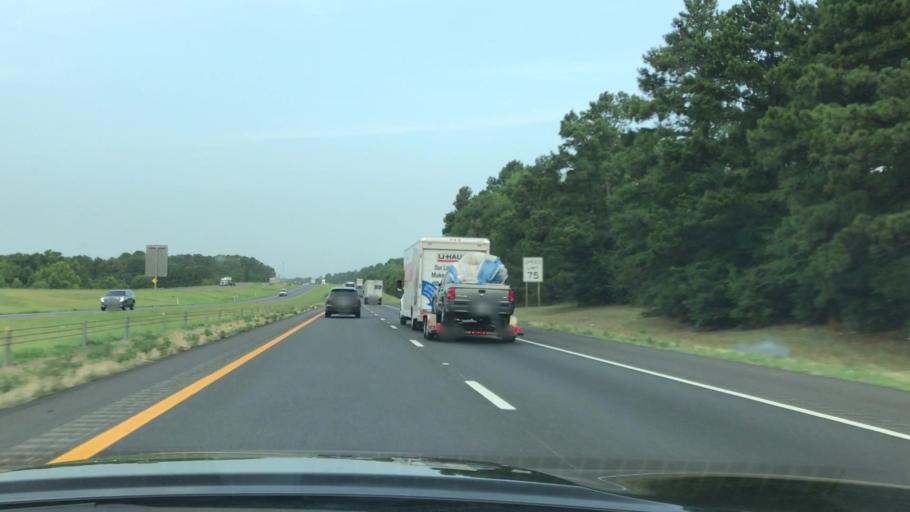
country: US
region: Texas
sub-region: Gregg County
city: Longview
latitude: 32.4586
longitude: -94.6785
